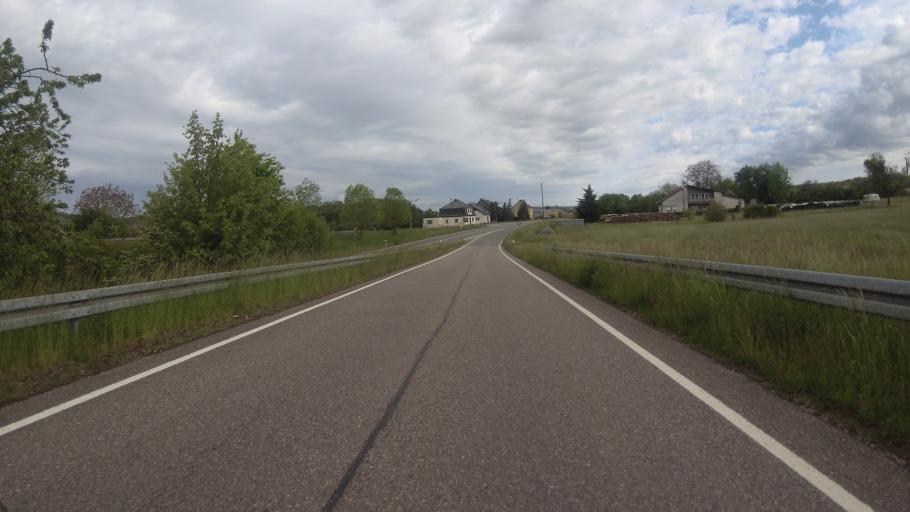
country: LU
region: Grevenmacher
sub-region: Canton de Remich
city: Remich
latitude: 49.5093
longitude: 6.3727
